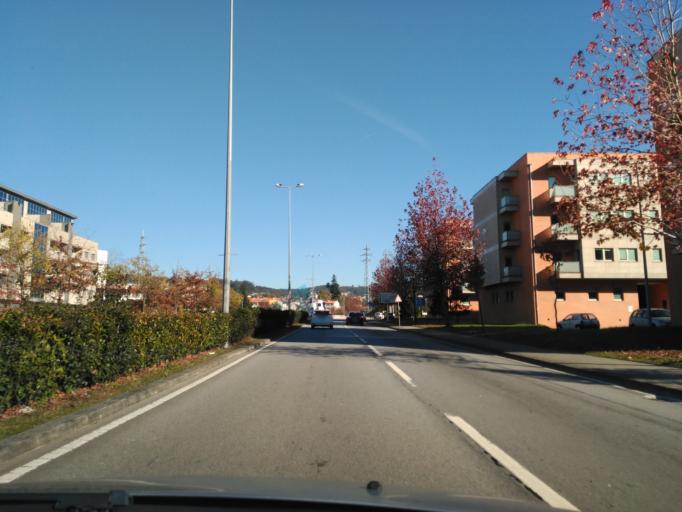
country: PT
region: Braga
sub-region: Braga
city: Adaufe
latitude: 41.5618
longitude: -8.3852
